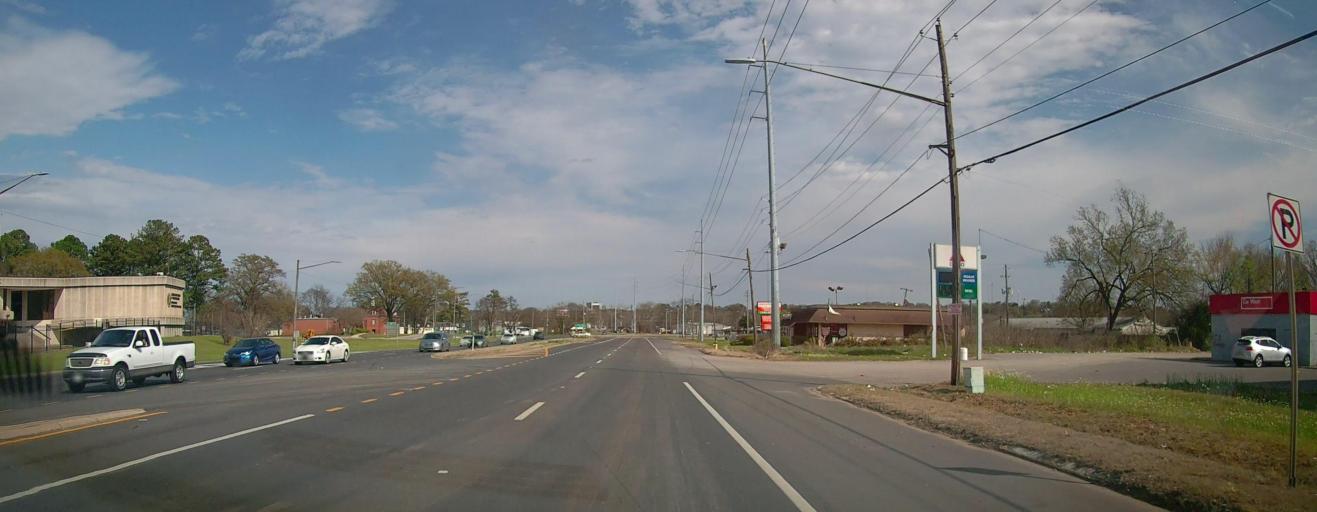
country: US
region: Alabama
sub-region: Jefferson County
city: Birmingham
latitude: 33.5317
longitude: -86.8546
